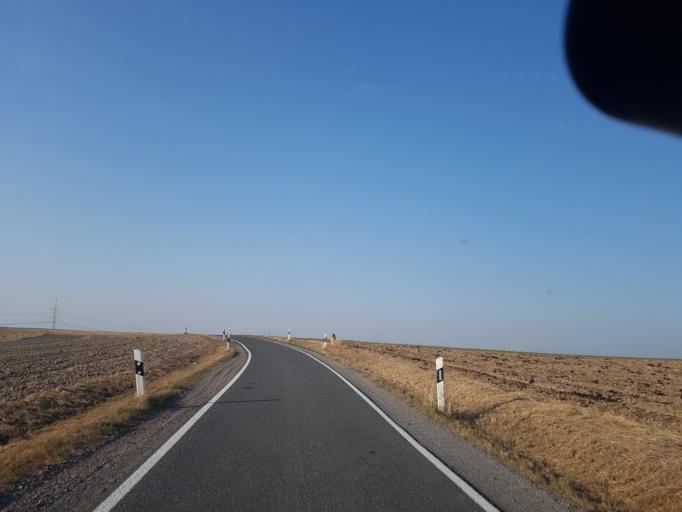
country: DE
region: Saxony
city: Stauchitz
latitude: 51.2943
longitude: 13.1916
